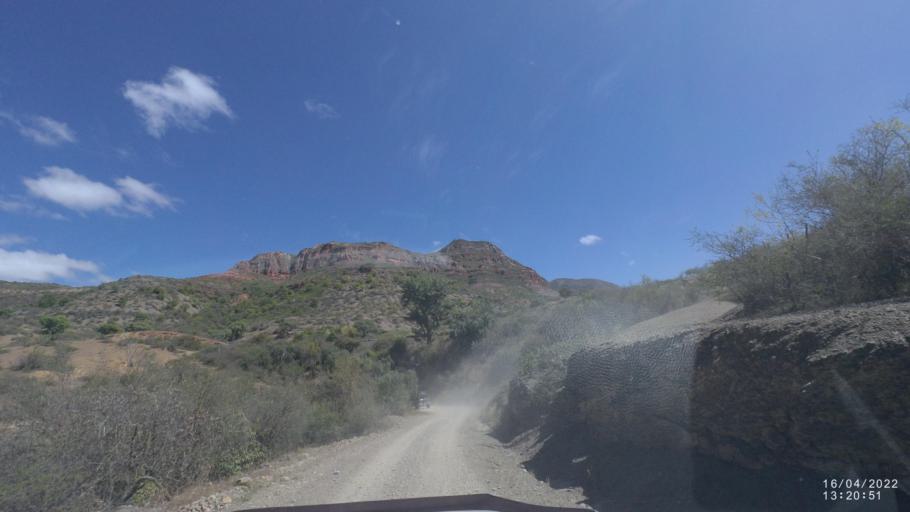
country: BO
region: Cochabamba
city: Mizque
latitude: -17.9907
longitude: -65.6122
